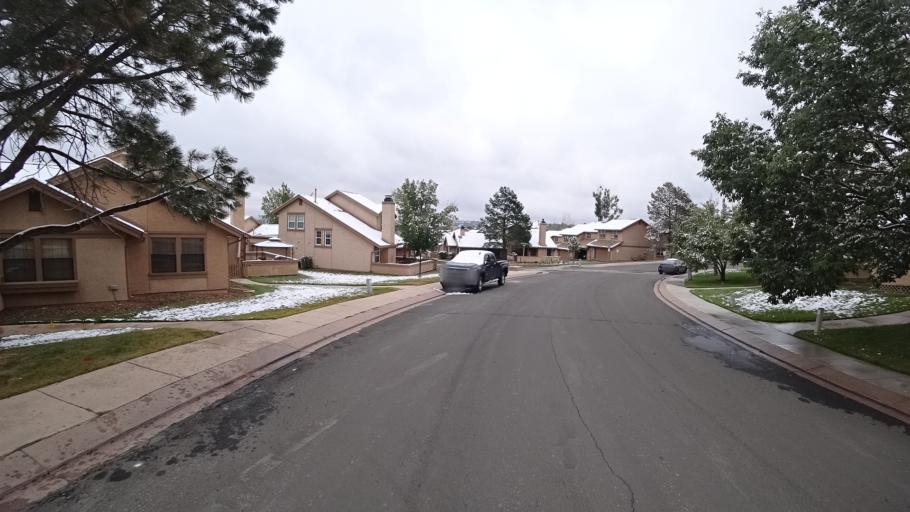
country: US
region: Colorado
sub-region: El Paso County
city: Colorado Springs
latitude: 38.9202
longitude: -104.7931
